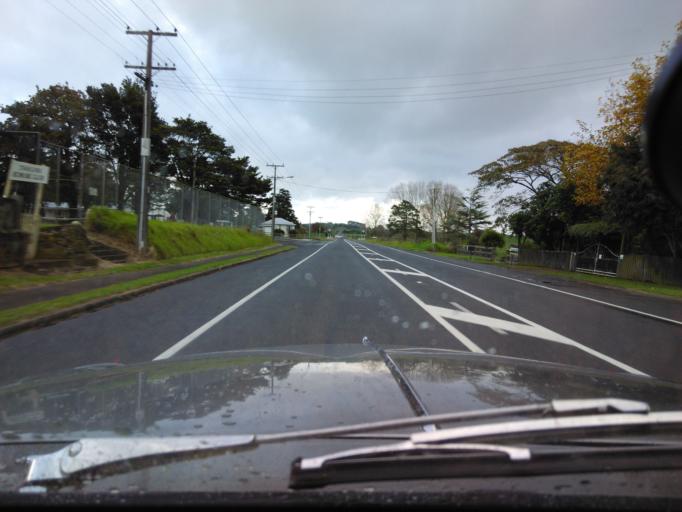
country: NZ
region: Waikato
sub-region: Hauraki District
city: Ngatea
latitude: -37.5008
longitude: 175.4905
